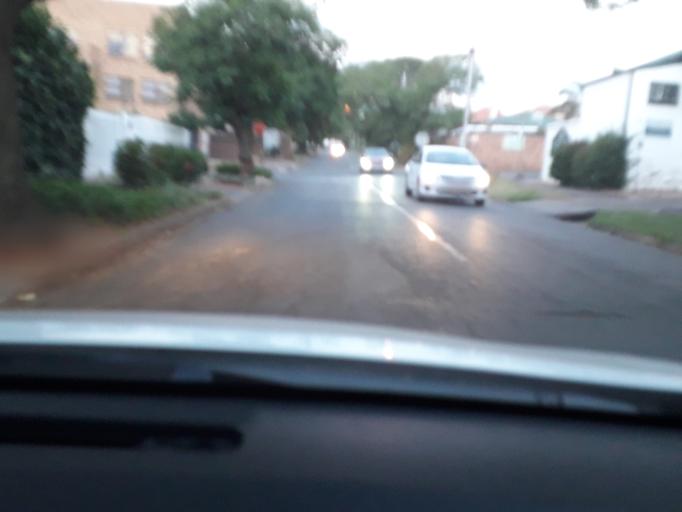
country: ZA
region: Gauteng
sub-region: City of Johannesburg Metropolitan Municipality
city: Johannesburg
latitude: -26.1806
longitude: 27.9944
